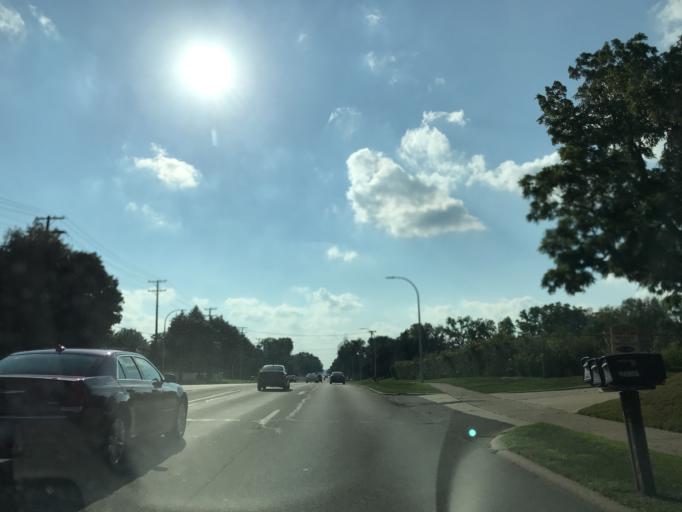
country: US
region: Michigan
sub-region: Wayne County
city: Livonia
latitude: 42.3970
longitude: -83.3866
